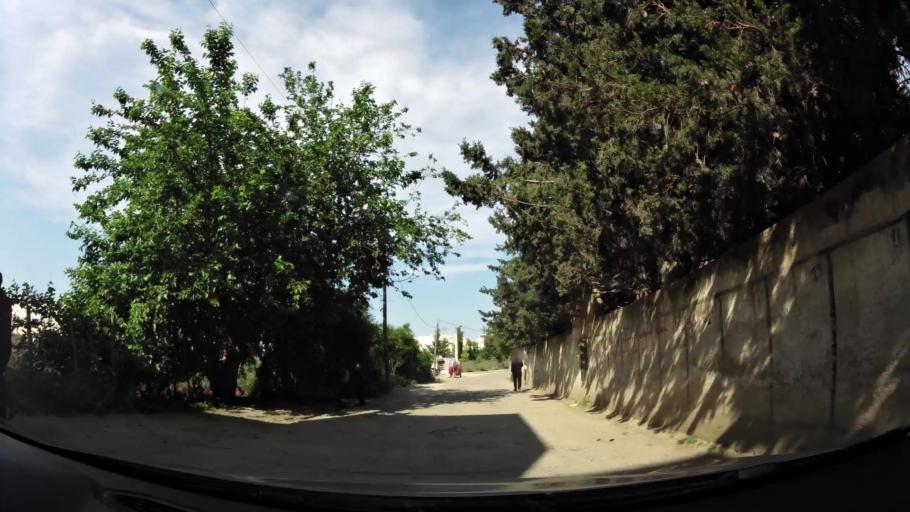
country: MA
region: Fes-Boulemane
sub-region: Fes
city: Fes
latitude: 34.0190
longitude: -5.0366
